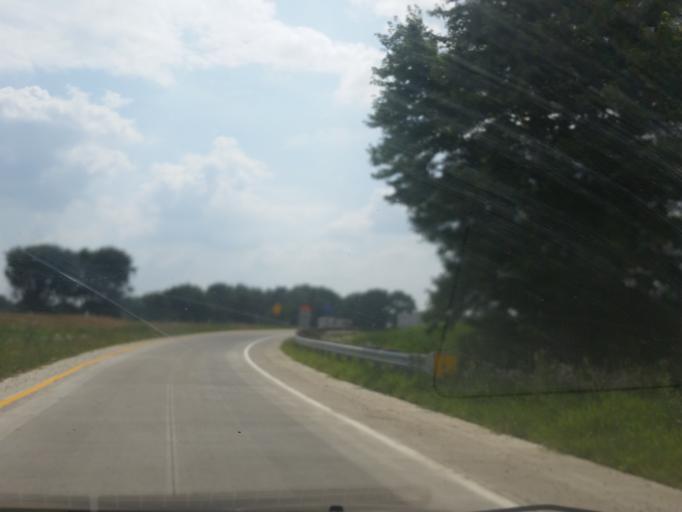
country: US
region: Ohio
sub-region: Summit County
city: Barberton
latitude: 41.0414
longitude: -81.6101
